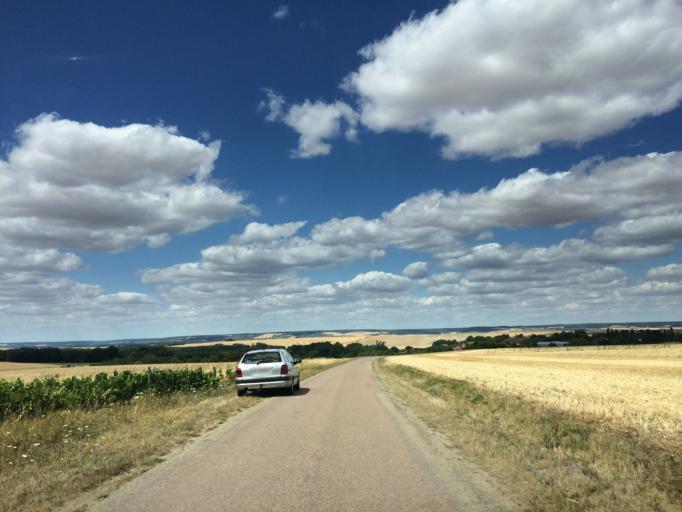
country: FR
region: Bourgogne
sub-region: Departement de l'Yonne
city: Fleury-la-Vallee
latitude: 47.9055
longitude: 3.4757
